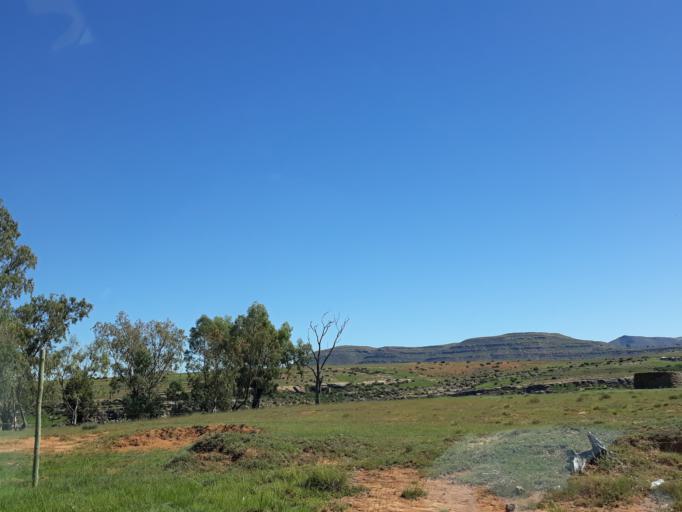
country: LS
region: Quthing
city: Quthing
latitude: -30.3403
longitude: 27.5291
